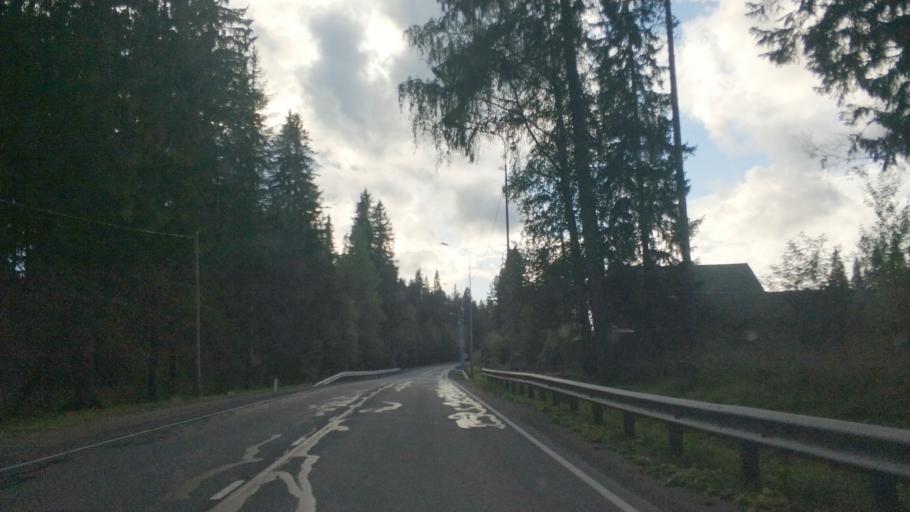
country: RU
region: Republic of Karelia
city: Lakhdenpokh'ya
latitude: 61.5143
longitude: 30.1227
